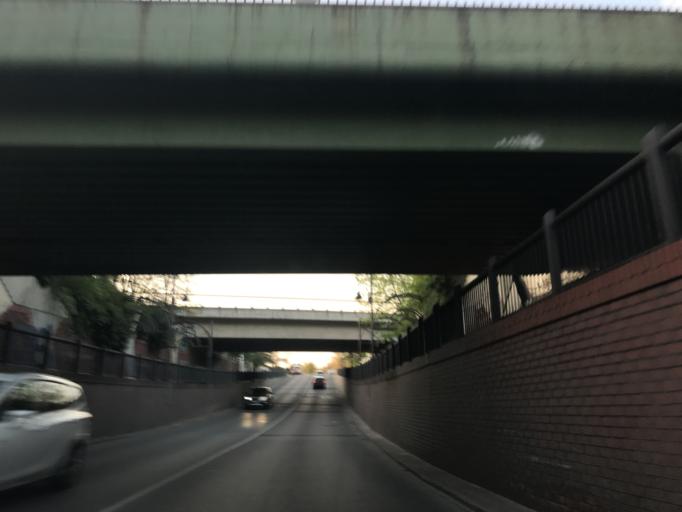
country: DE
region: Berlin
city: Staaken
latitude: 52.5365
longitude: 13.1567
